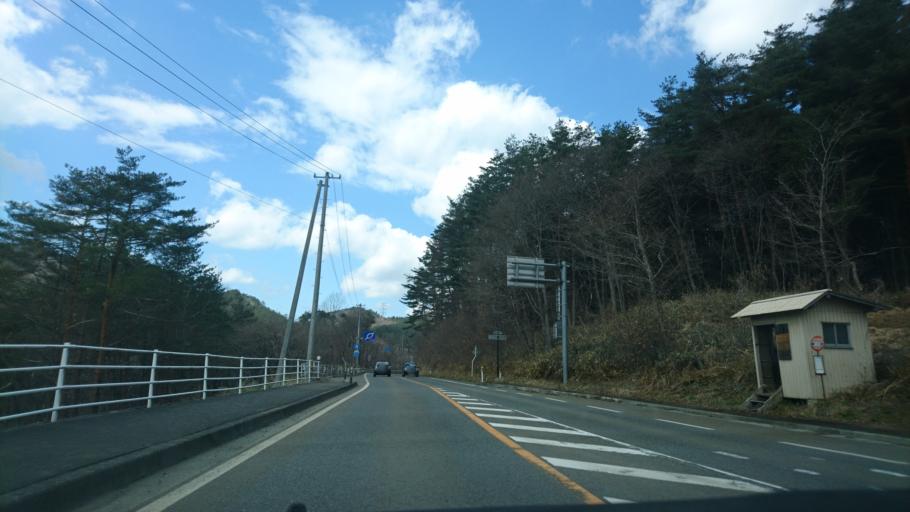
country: JP
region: Iwate
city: Tono
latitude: 39.3116
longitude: 141.3725
